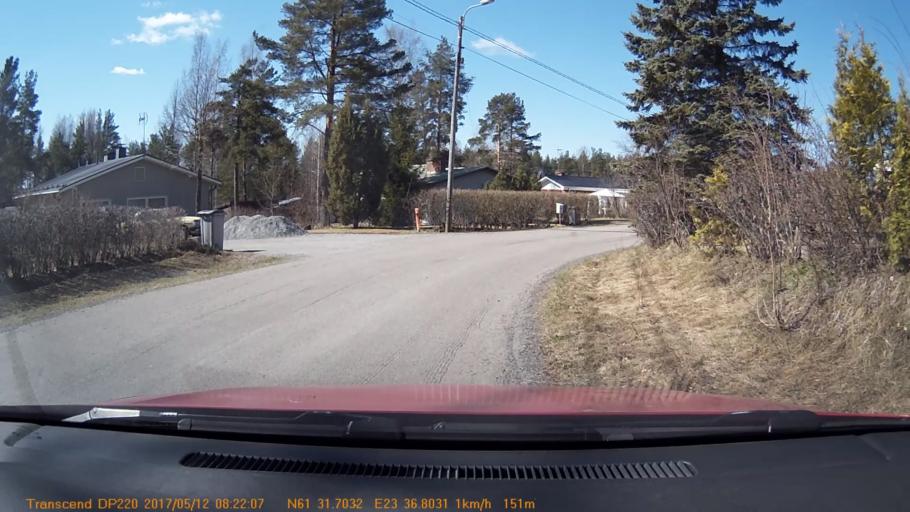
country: FI
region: Pirkanmaa
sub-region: Tampere
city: Yloejaervi
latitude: 61.5284
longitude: 23.6134
